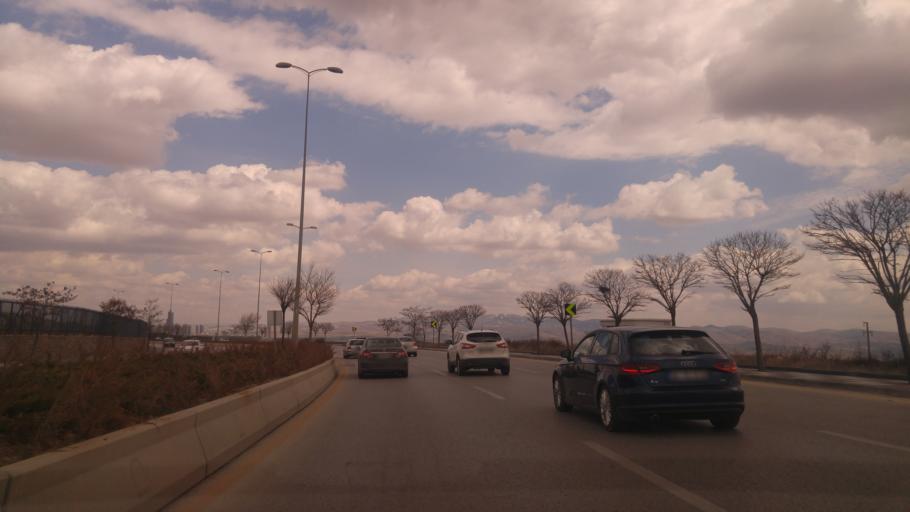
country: TR
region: Ankara
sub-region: Goelbasi
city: Golbasi
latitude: 39.8355
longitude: 32.7678
